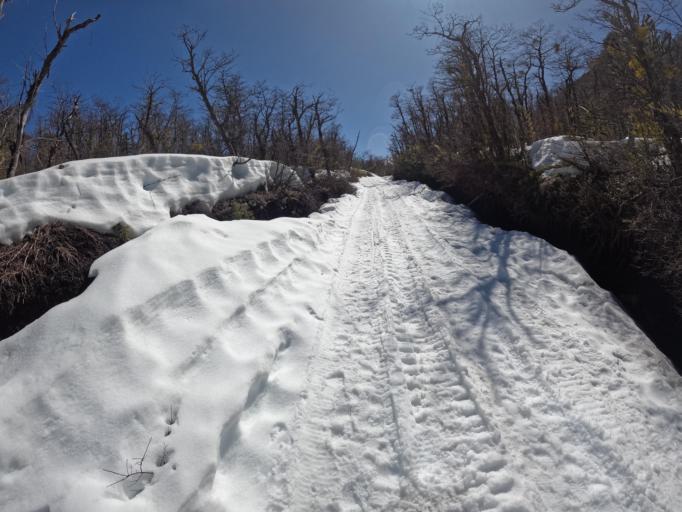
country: CL
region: Araucania
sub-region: Provincia de Cautin
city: Vilcun
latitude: -38.6620
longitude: -71.6186
